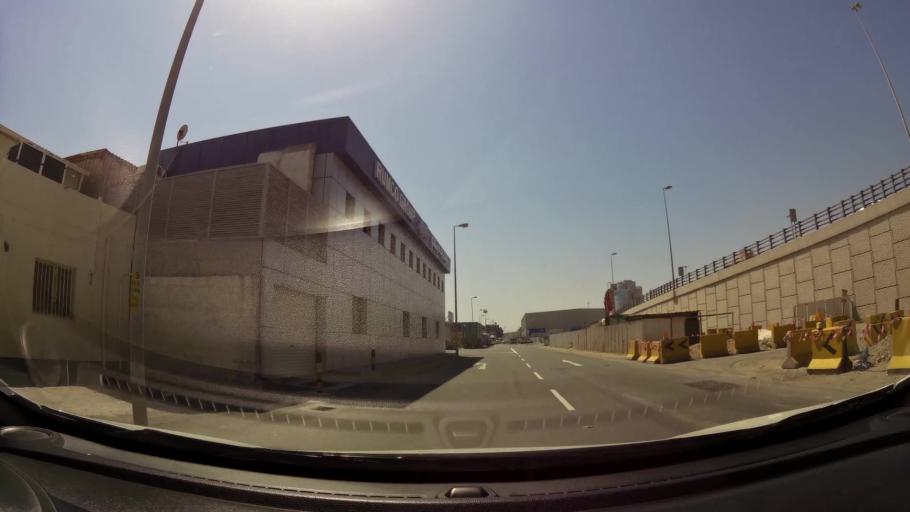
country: BH
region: Manama
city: Manama
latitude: 26.2016
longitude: 50.6014
